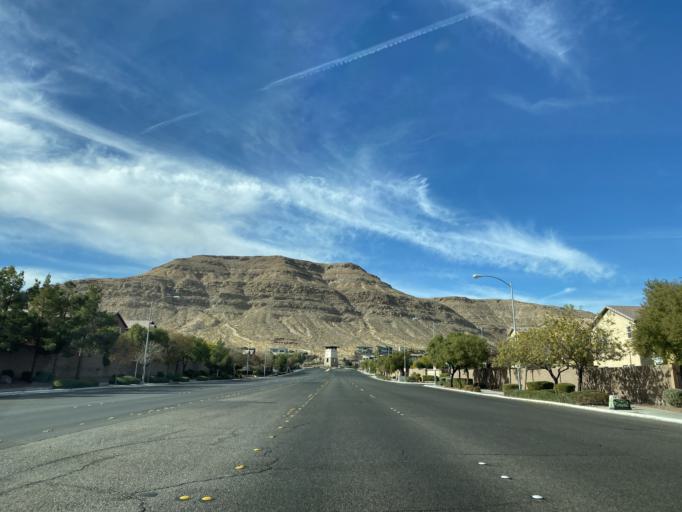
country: US
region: Nevada
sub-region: Clark County
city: Summerlin South
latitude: 36.0701
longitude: -115.3117
